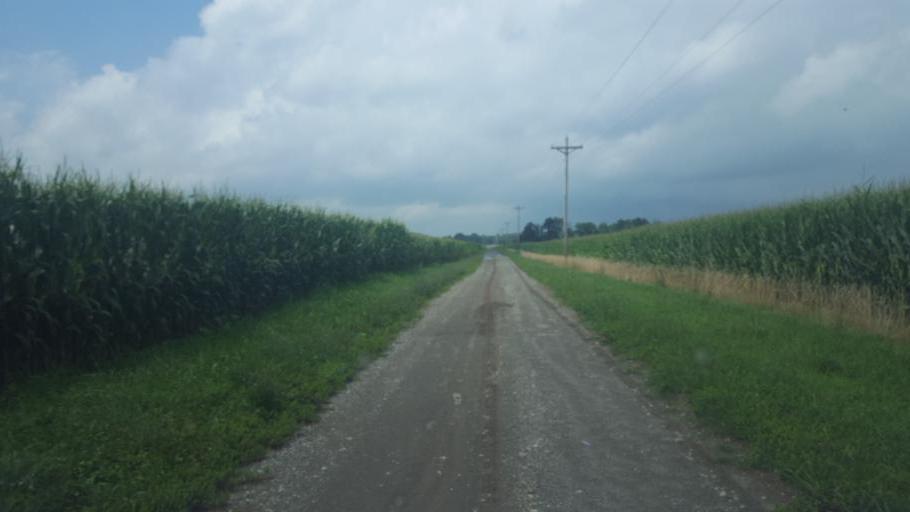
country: US
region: Ohio
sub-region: Union County
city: Richwood
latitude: 40.5382
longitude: -83.3335
